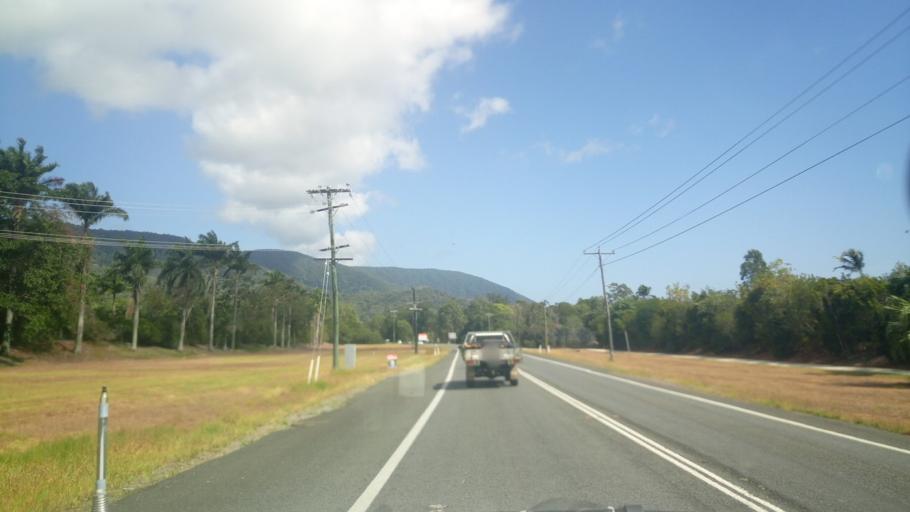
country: AU
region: Queensland
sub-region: Cairns
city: Trinity Beach
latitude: -16.7903
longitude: 145.6774
